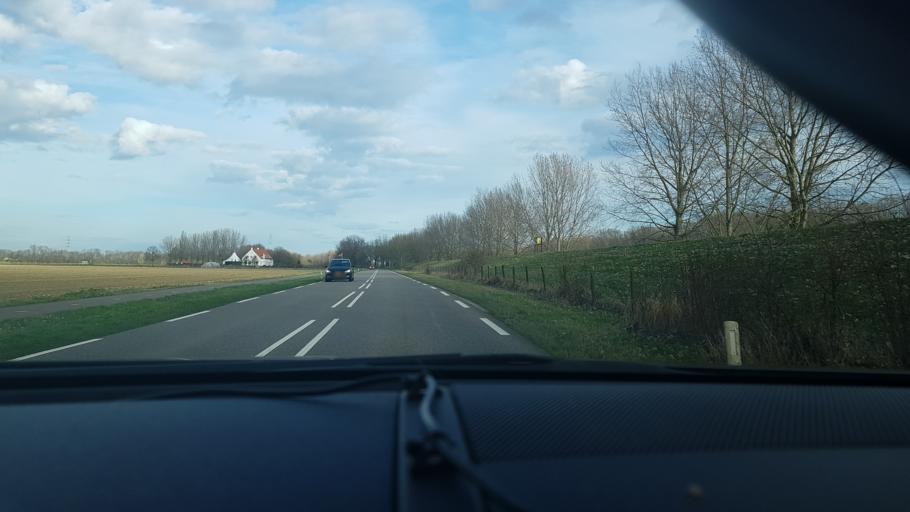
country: NL
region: Limburg
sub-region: Gemeente Leudal
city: Haelen
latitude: 51.2096
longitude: 5.9647
